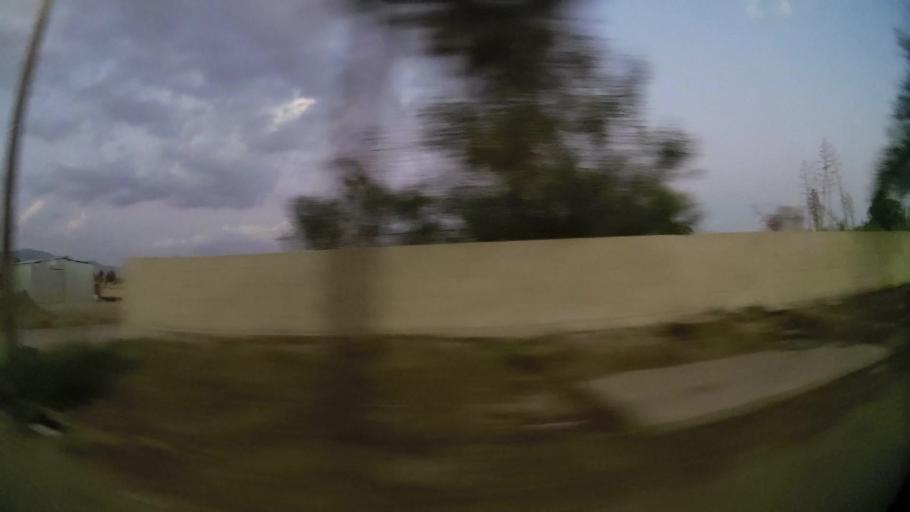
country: CY
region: Lefkosia
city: Nicosia
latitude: 35.1924
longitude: 33.3736
